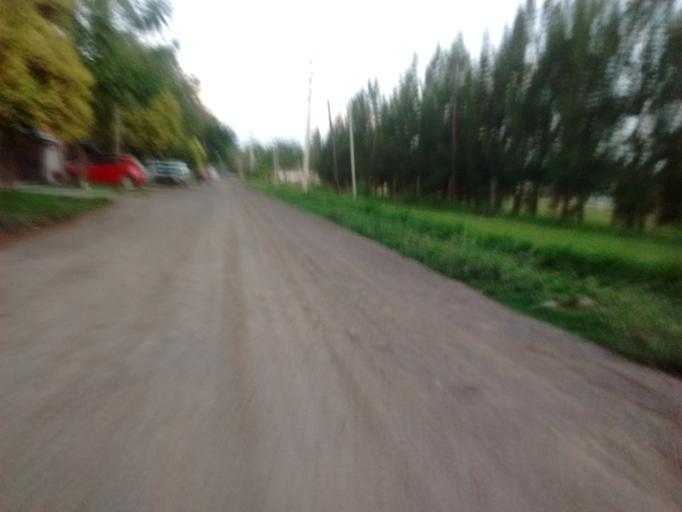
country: AR
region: Santa Fe
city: Funes
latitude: -32.9107
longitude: -60.8081
